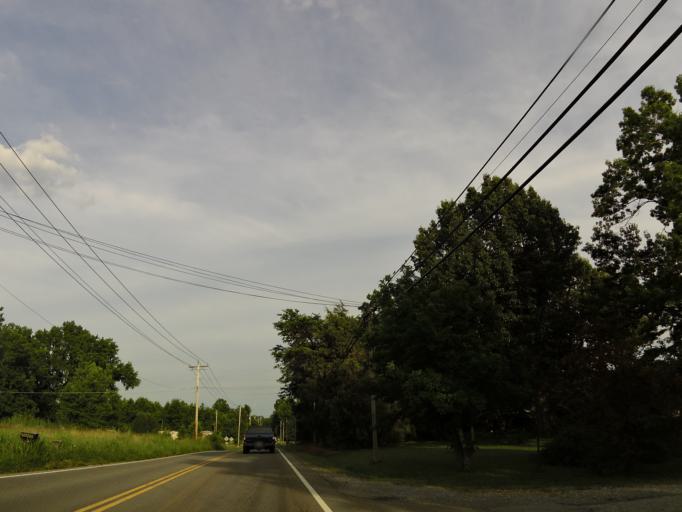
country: US
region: Tennessee
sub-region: Dickson County
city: Burns
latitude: 36.0606
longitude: -87.3401
